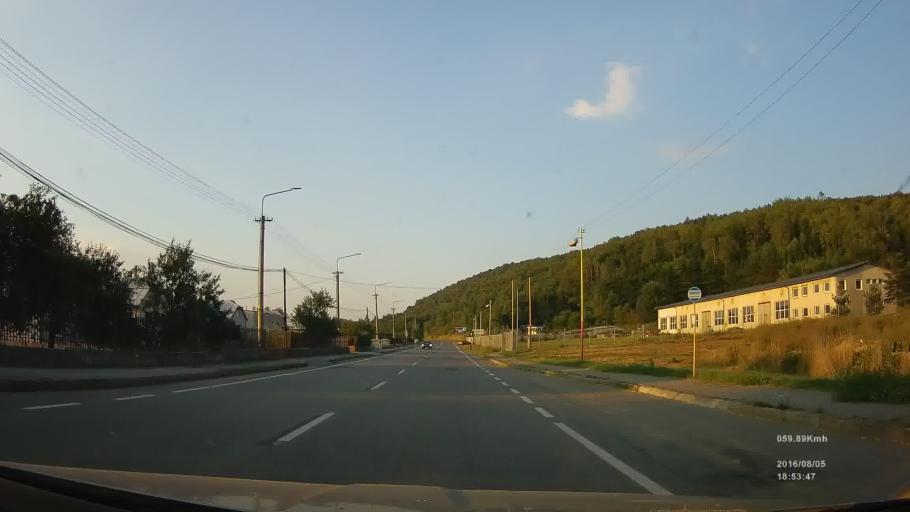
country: SK
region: Presovsky
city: Stropkov
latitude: 49.2192
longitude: 21.6611
